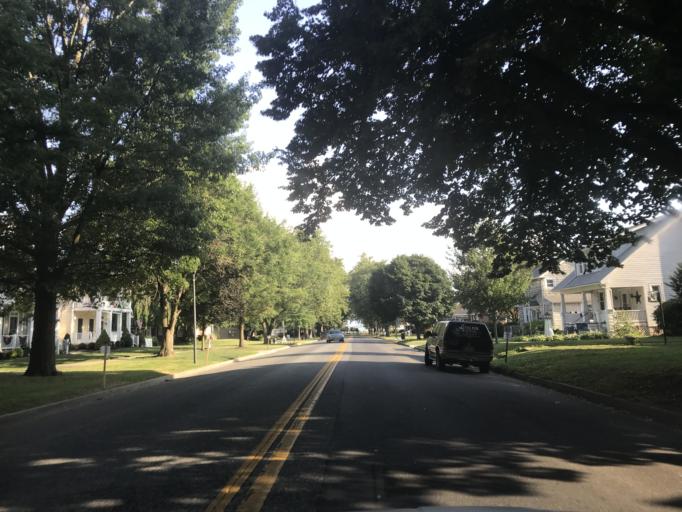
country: US
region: Maryland
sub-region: Harford County
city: Havre de Grace
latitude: 39.5414
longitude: -76.0915
